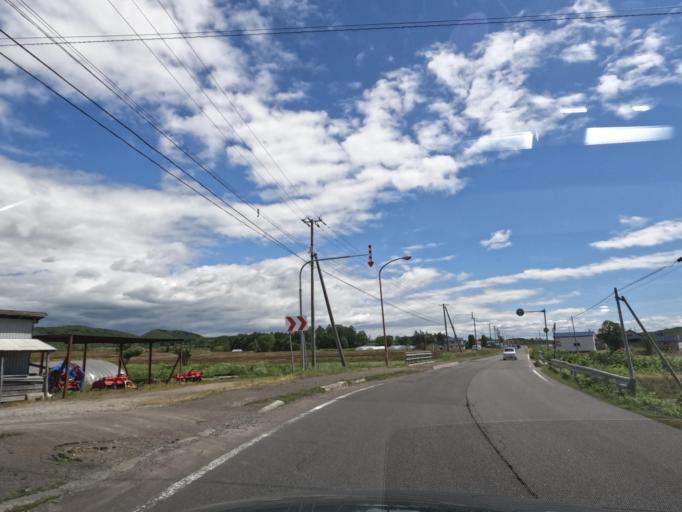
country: JP
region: Hokkaido
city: Iwamizawa
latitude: 43.1429
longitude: 141.8053
